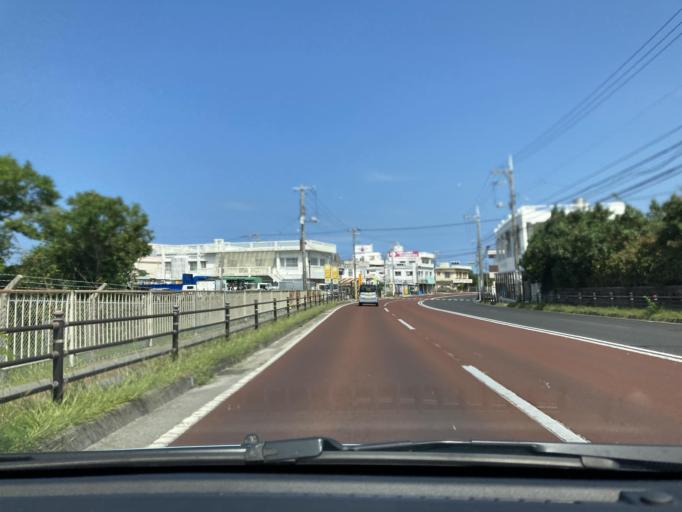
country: JP
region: Okinawa
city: Ginowan
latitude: 26.2836
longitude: 127.7766
